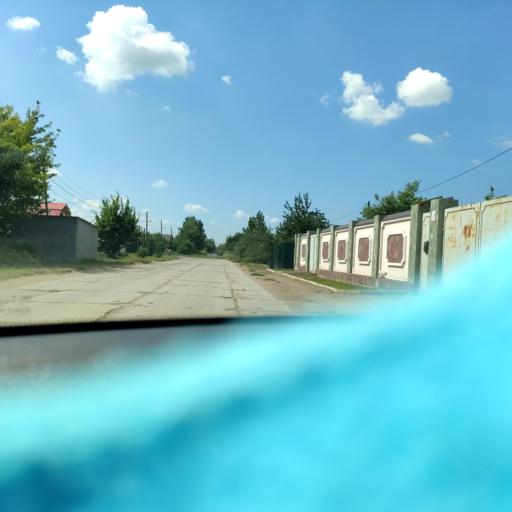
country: RU
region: Samara
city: Smyshlyayevka
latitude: 53.2230
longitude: 50.3389
